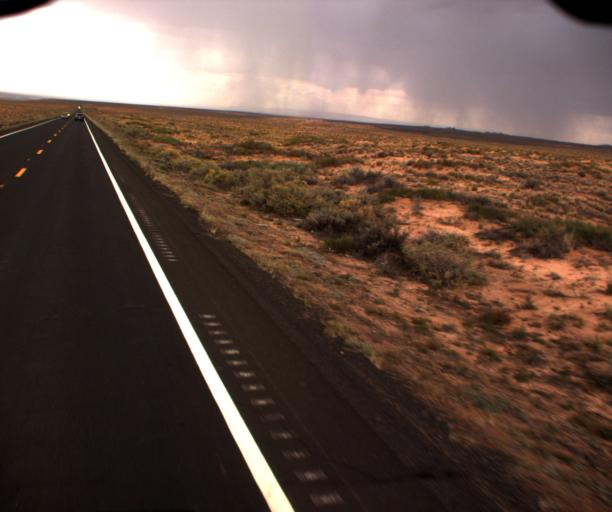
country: US
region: Arizona
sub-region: Coconino County
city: Tuba City
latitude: 36.2072
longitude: -111.0528
